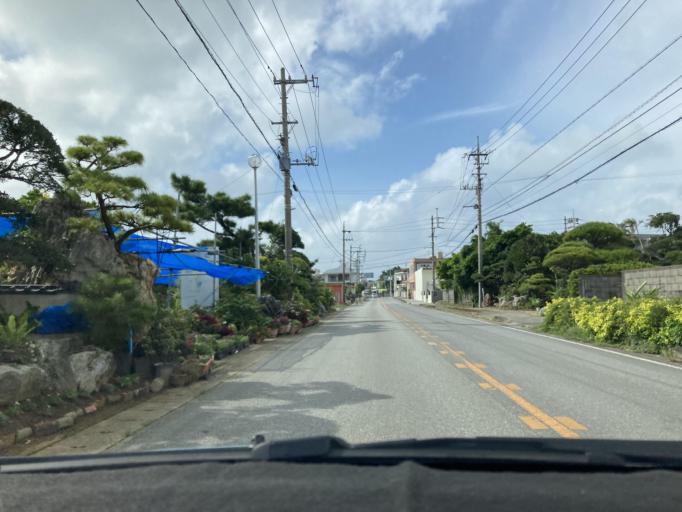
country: JP
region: Okinawa
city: Itoman
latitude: 26.1039
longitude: 127.6681
